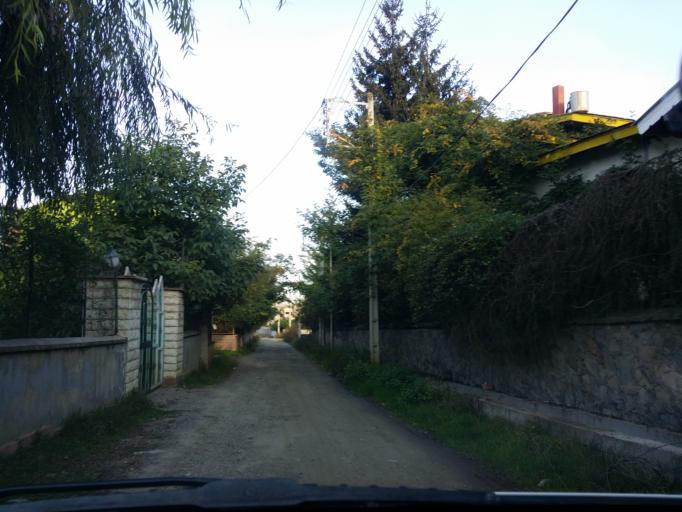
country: IR
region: Mazandaran
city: `Abbasabad
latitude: 36.5098
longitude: 51.1728
